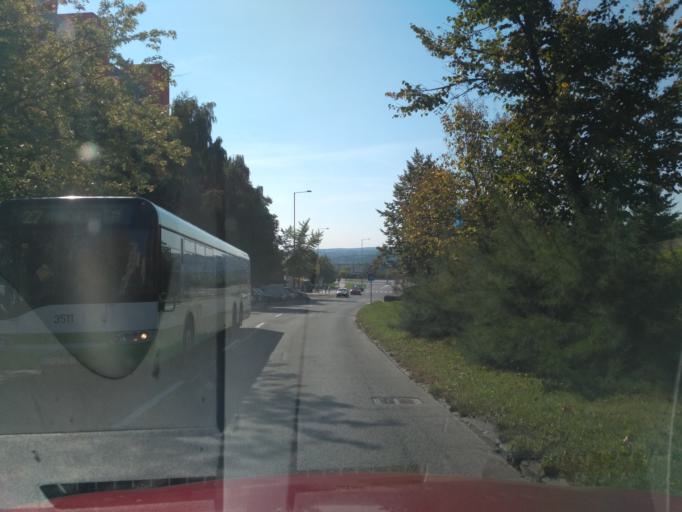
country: SK
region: Kosicky
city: Kosice
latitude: 48.7571
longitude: 21.2677
